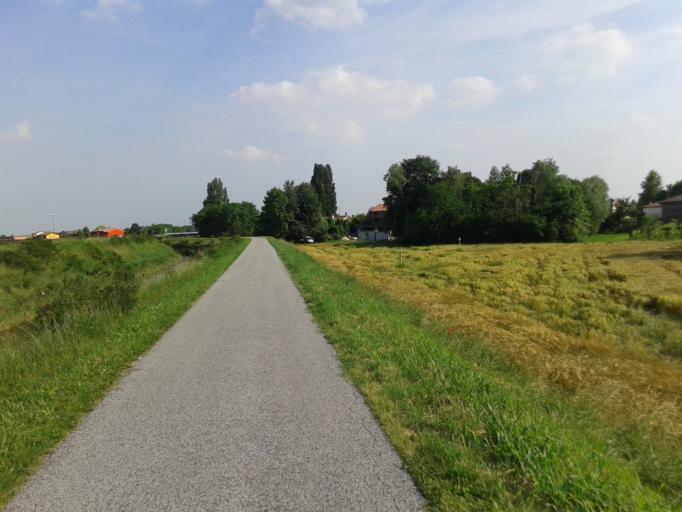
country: IT
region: Veneto
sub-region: Provincia di Padova
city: Loreggiola
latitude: 45.6036
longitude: 11.9322
